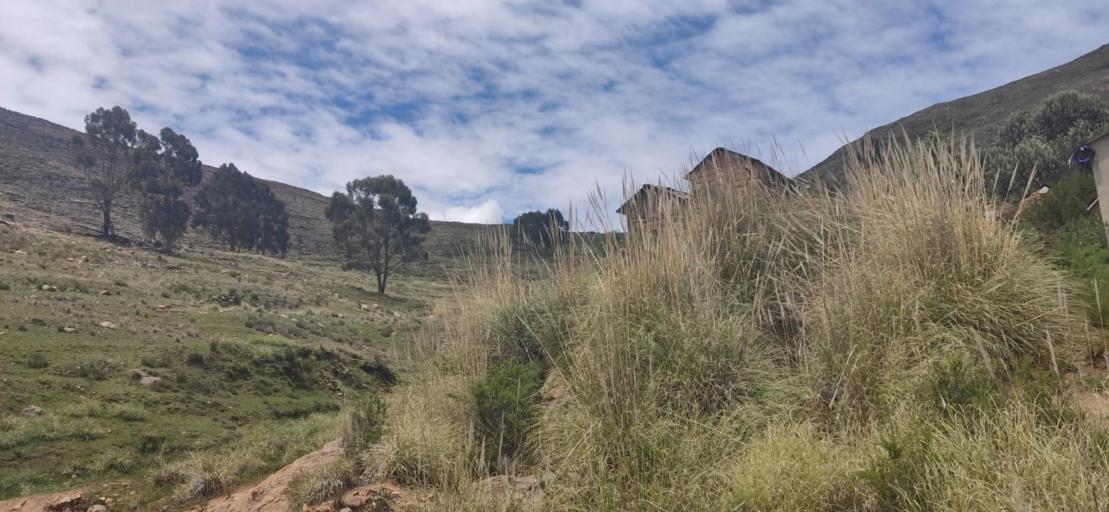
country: BO
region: La Paz
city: Batallas
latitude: -16.3471
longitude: -68.6463
